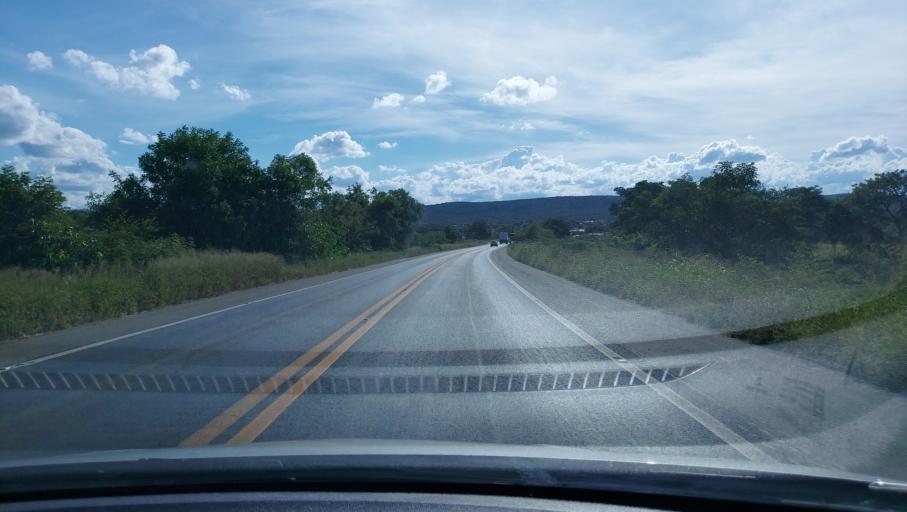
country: BR
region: Bahia
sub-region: Seabra
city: Seabra
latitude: -12.4841
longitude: -41.7227
